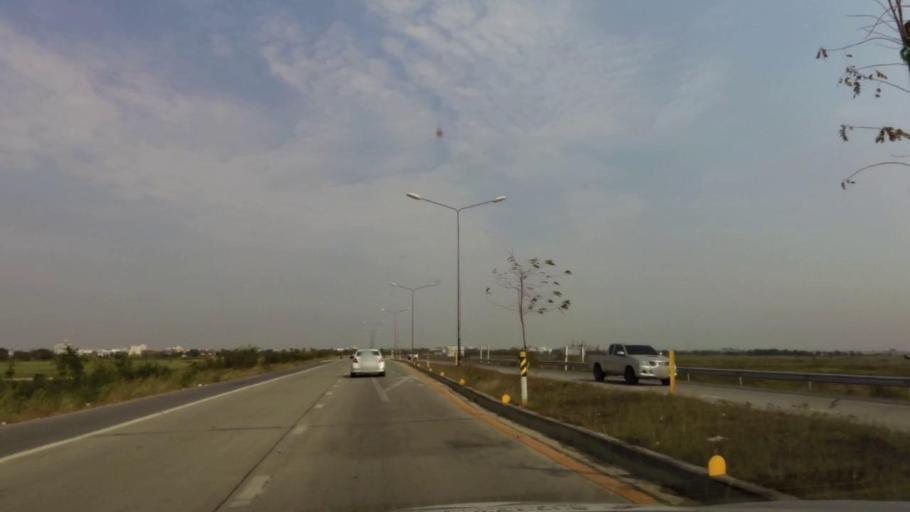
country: TH
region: Phra Nakhon Si Ayutthaya
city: Phra Nakhon Si Ayutthaya
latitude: 14.3318
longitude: 100.5912
